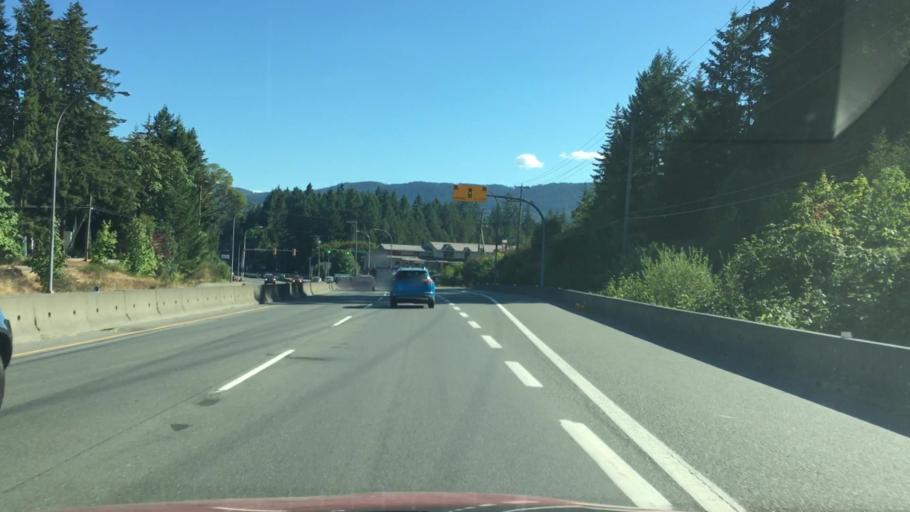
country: CA
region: British Columbia
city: North Saanich
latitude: 48.6590
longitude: -123.5606
